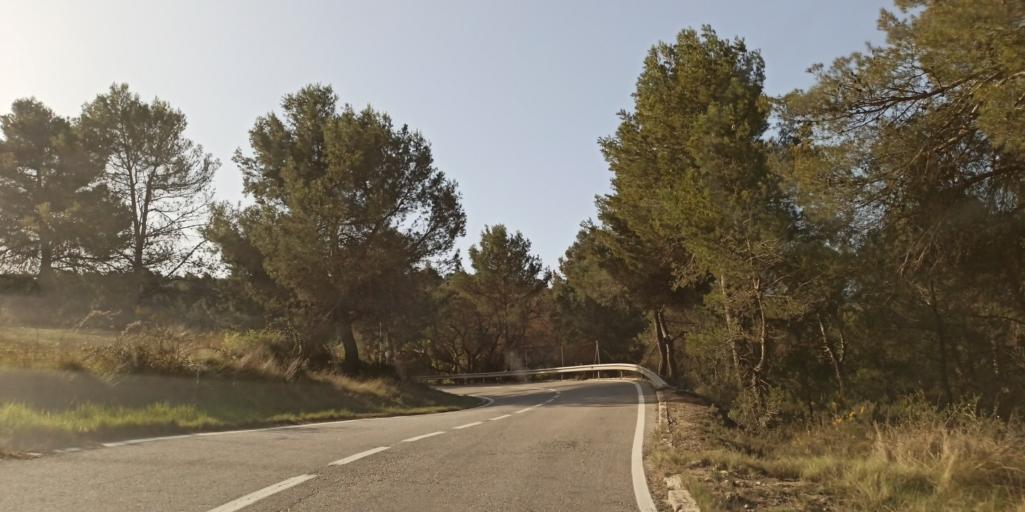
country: ES
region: Catalonia
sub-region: Provincia de Barcelona
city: Castelloli
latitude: 41.5976
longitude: 1.7085
